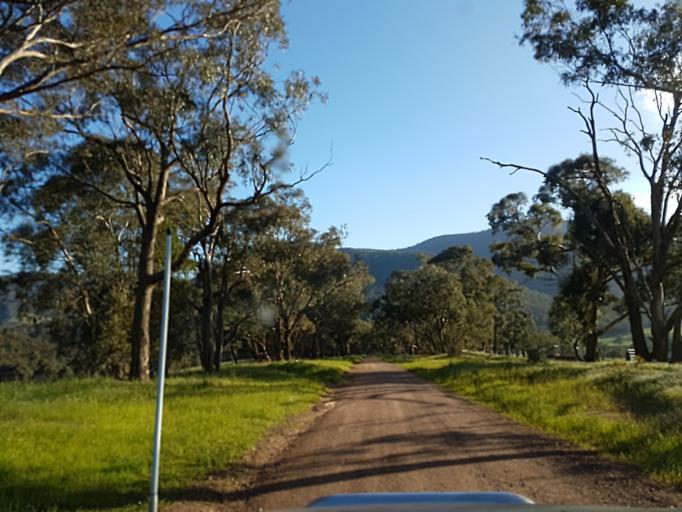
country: AU
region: Victoria
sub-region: East Gippsland
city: Bairnsdale
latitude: -37.4900
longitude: 147.1897
